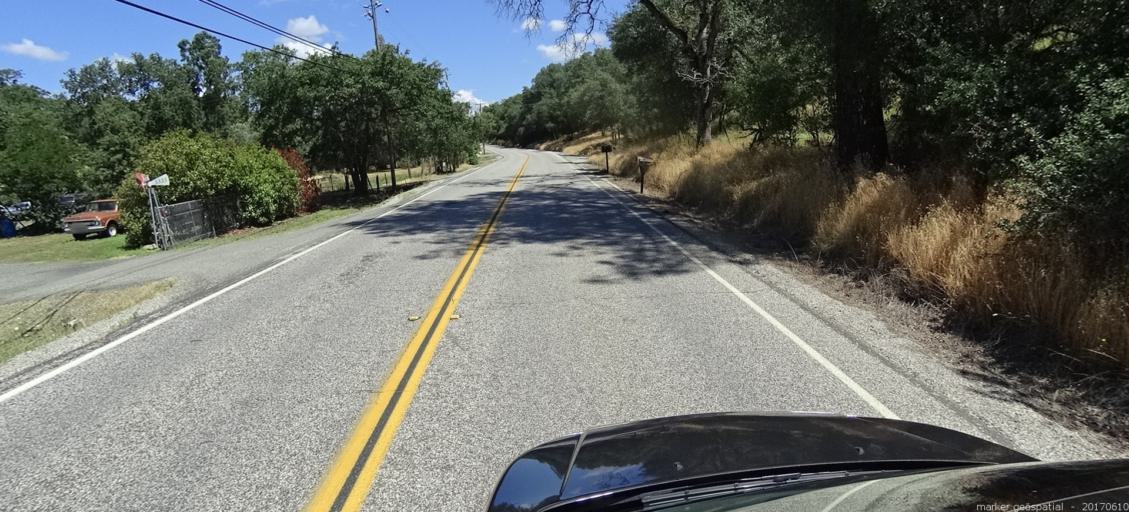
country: US
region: California
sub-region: Butte County
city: Oroville East
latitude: 39.4796
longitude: -121.4578
